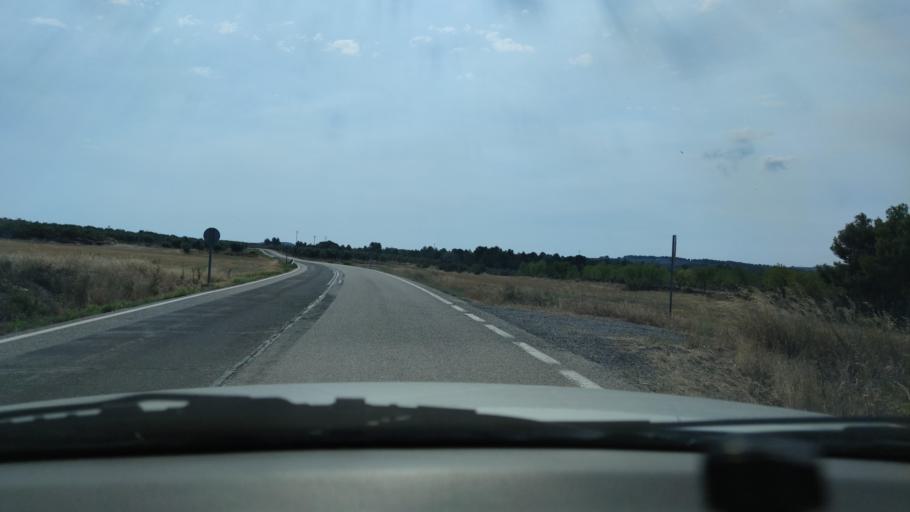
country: ES
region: Catalonia
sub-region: Provincia de Lleida
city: Arbeca
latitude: 41.5025
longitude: 0.9419
